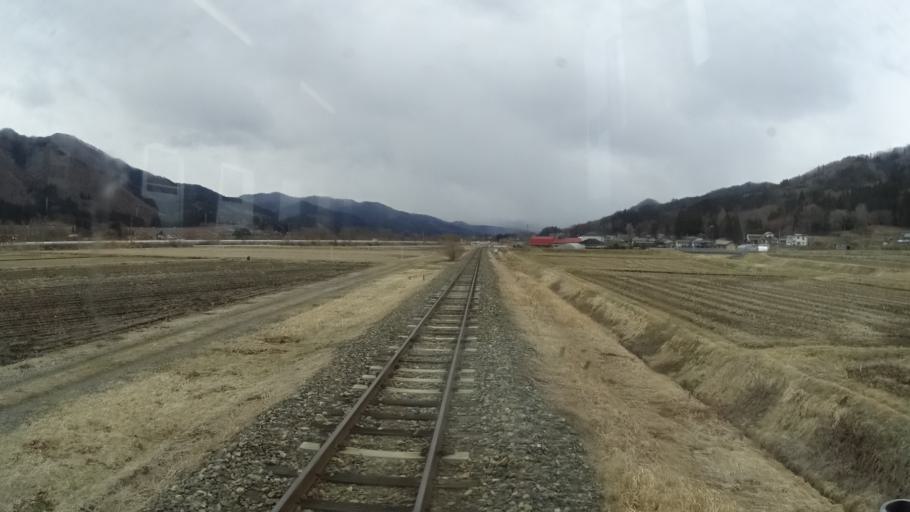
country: JP
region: Iwate
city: Tono
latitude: 39.3215
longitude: 141.4503
